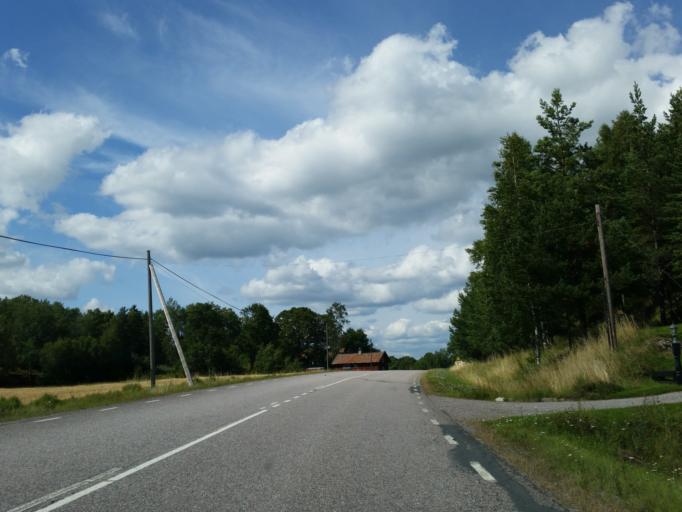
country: SE
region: Soedermanland
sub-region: Trosa Kommun
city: Vagnharad
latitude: 59.0001
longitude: 17.6049
